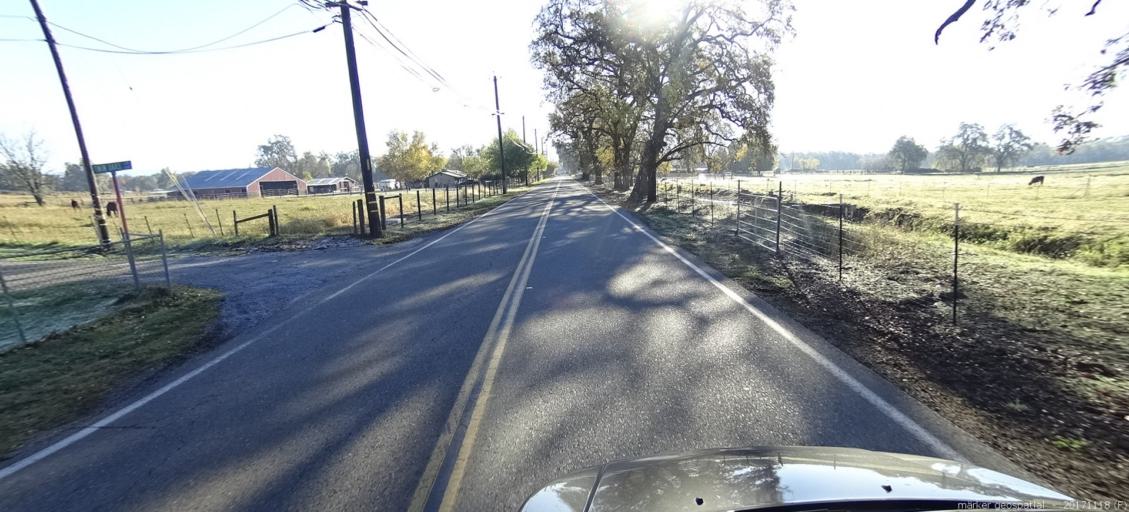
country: US
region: California
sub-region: Shasta County
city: Anderson
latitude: 40.4506
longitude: -122.2668
